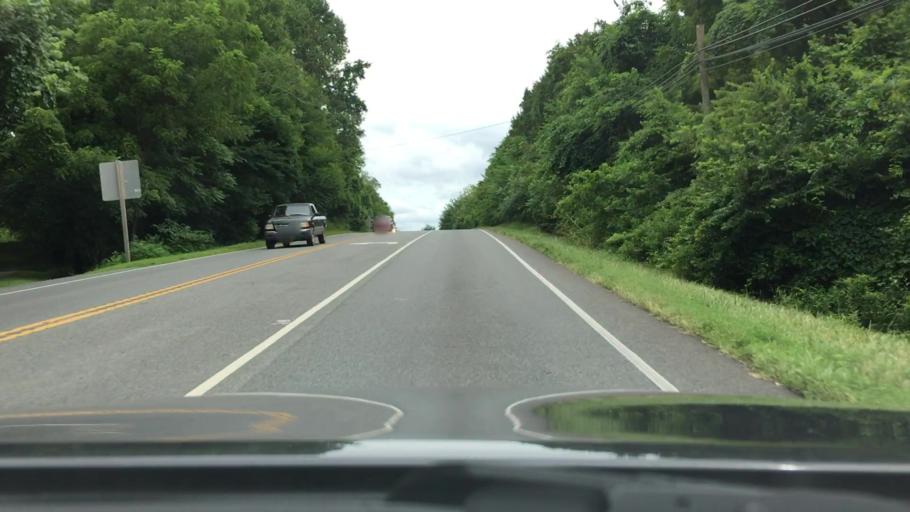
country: US
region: Virginia
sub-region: City of Charlottesville
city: Charlottesville
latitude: 38.0161
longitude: -78.4236
